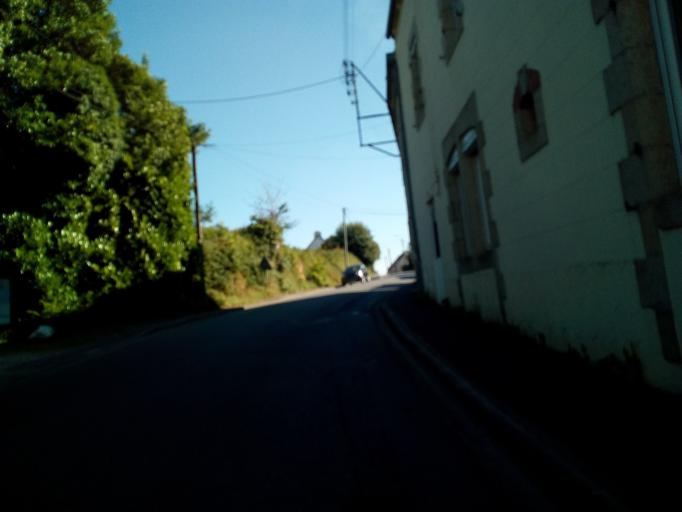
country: FR
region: Brittany
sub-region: Departement du Finistere
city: Landivisiau
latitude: 48.5043
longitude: -4.0769
